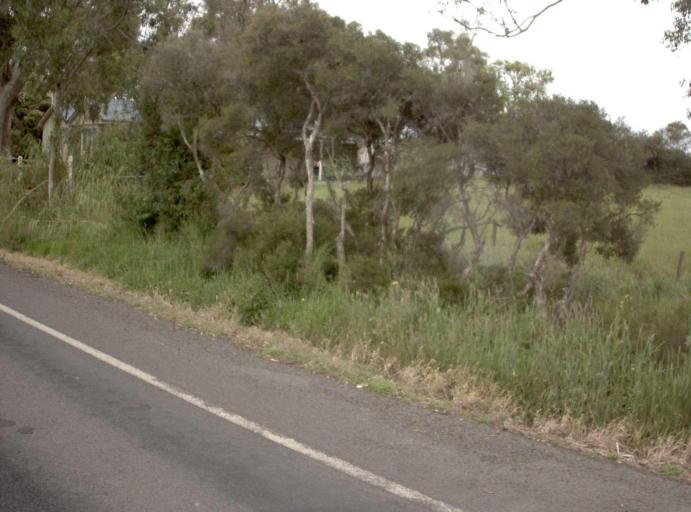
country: AU
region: Victoria
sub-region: Baw Baw
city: Warragul
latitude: -38.5002
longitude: 145.9519
